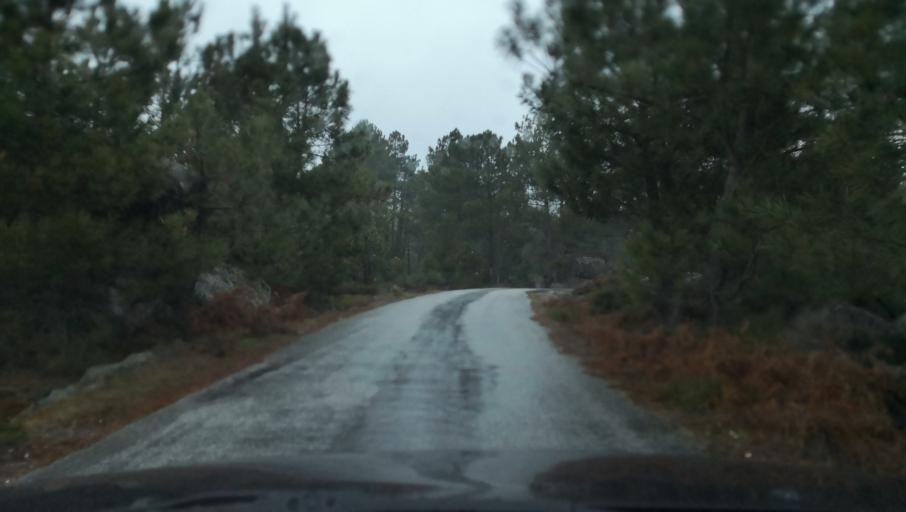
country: PT
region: Vila Real
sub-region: Vila Real
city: Vila Real
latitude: 41.3328
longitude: -7.7870
